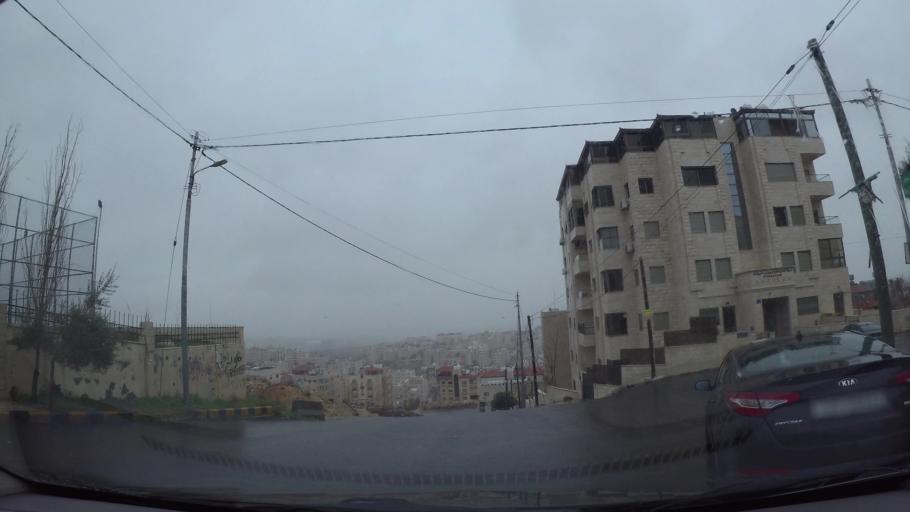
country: JO
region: Amman
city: Al Jubayhah
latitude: 32.0209
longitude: 35.8883
